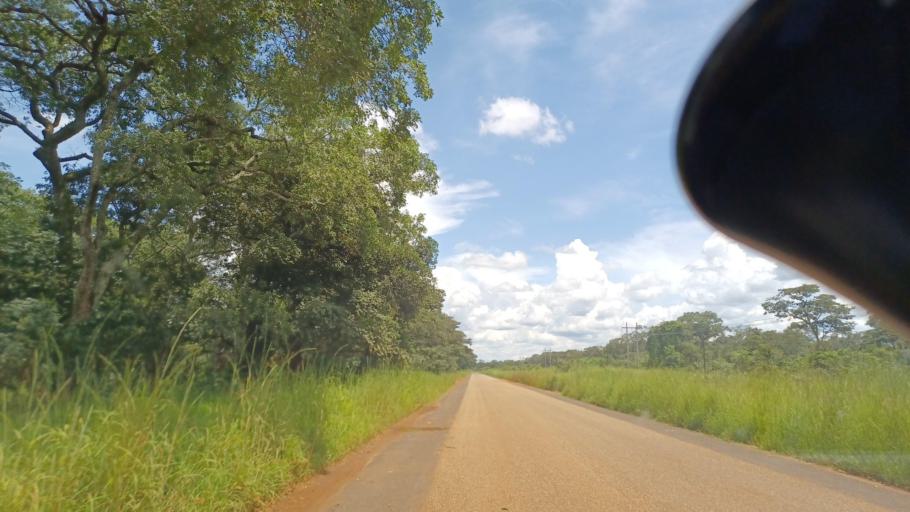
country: ZM
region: North-Western
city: Solwezi
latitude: -12.5742
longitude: 26.1339
